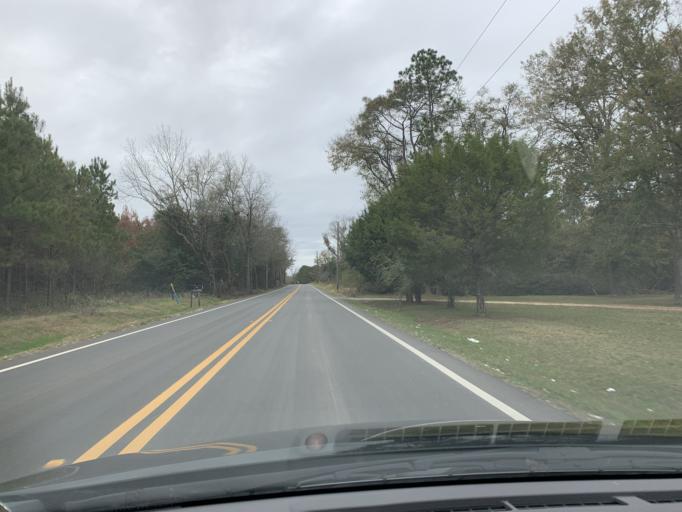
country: US
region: Georgia
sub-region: Thomas County
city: Meigs
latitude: 31.0084
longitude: -84.0618
